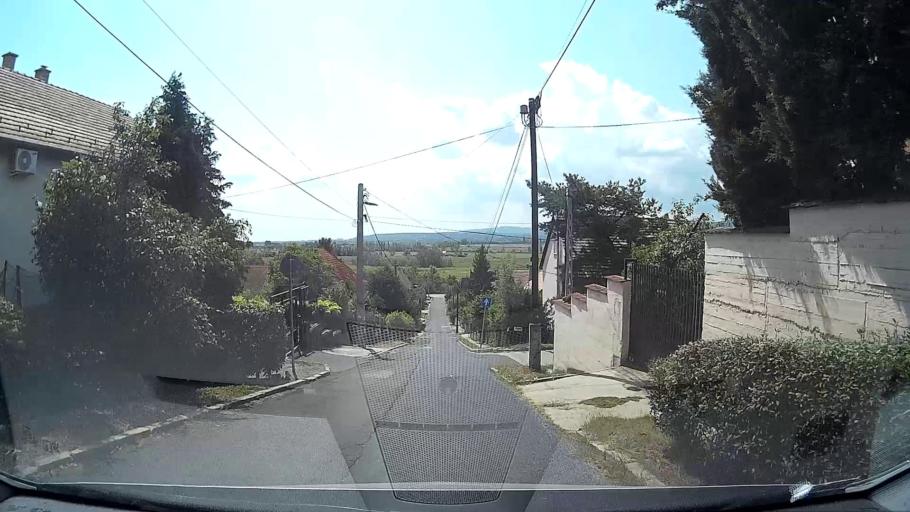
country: HU
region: Pest
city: Szentendre
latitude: 47.6656
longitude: 19.0597
